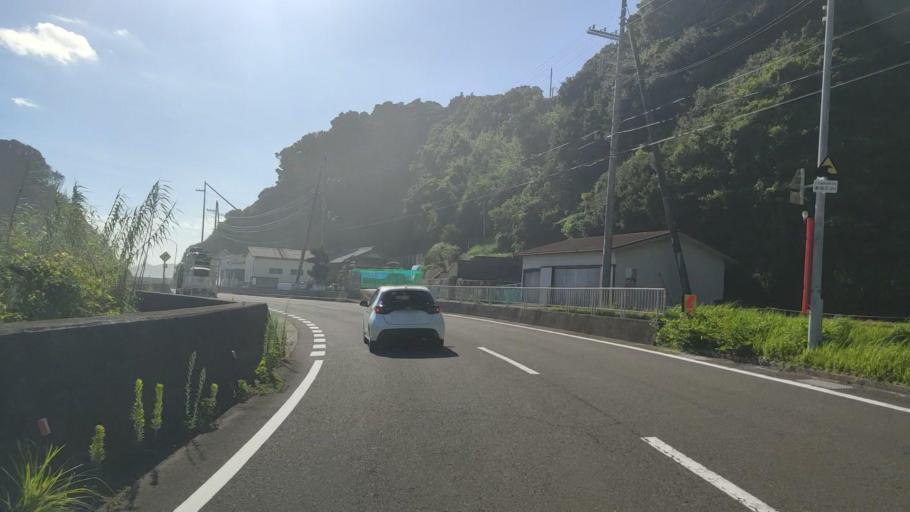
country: JP
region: Wakayama
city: Tanabe
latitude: 33.5034
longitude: 135.6417
